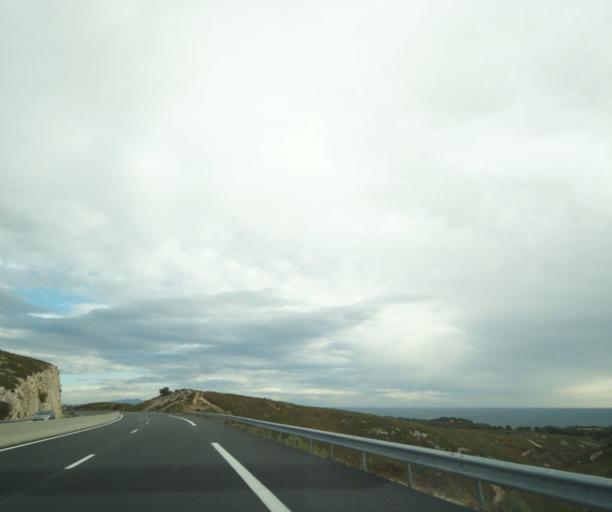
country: FR
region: Provence-Alpes-Cote d'Azur
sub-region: Departement des Bouches-du-Rhone
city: Carry-le-Rouet
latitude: 43.3398
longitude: 5.1362
